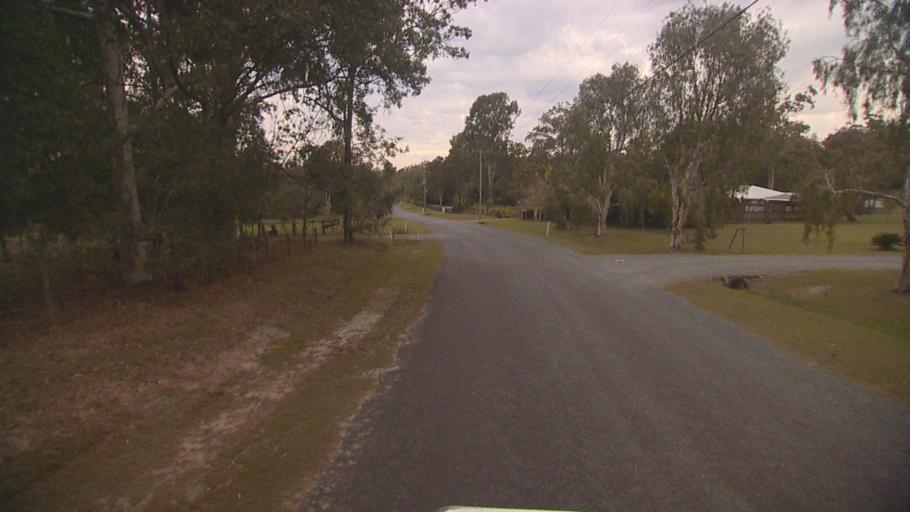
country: AU
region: Queensland
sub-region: Logan
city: Chambers Flat
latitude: -27.7903
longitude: 153.1108
